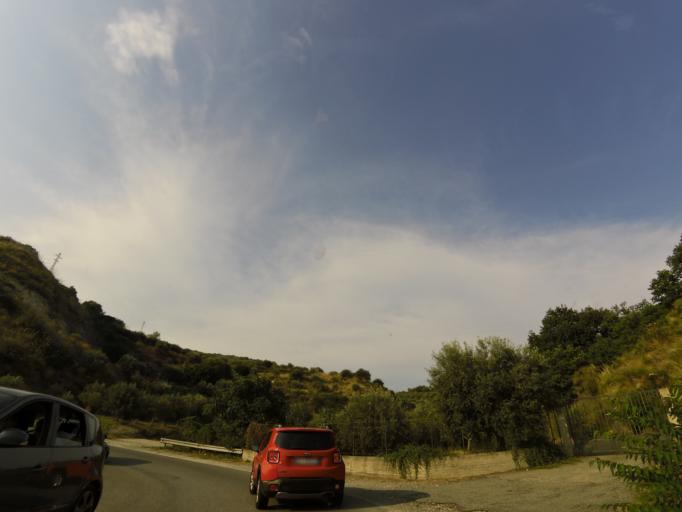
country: IT
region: Calabria
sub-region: Provincia di Reggio Calabria
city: Monasterace
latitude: 38.4586
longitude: 16.5233
